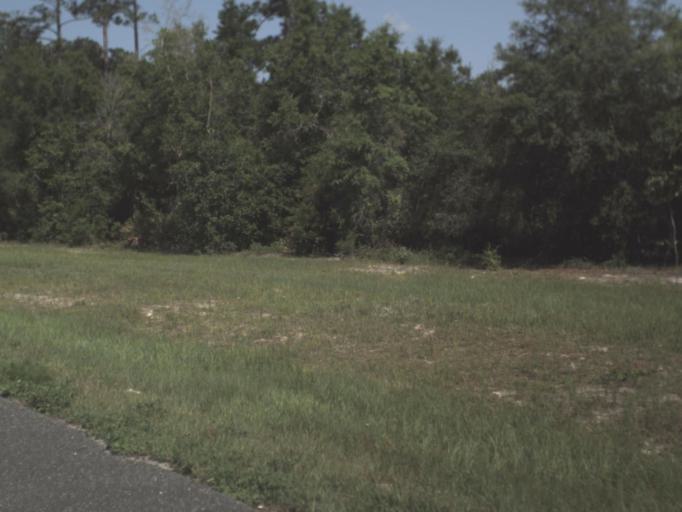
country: US
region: Florida
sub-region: Clay County
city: Green Cove Springs
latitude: 29.9835
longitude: -81.7418
